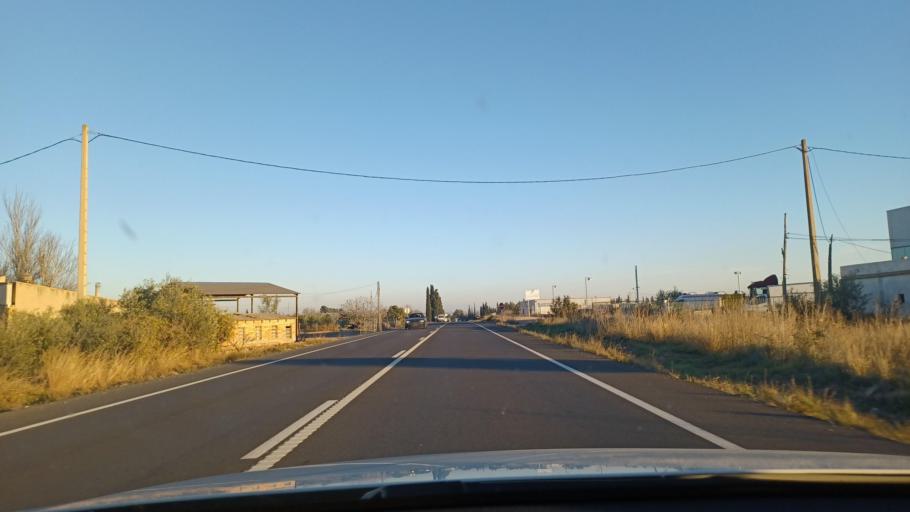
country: ES
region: Catalonia
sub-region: Provincia de Tarragona
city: Amposta
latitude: 40.6985
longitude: 0.5705
